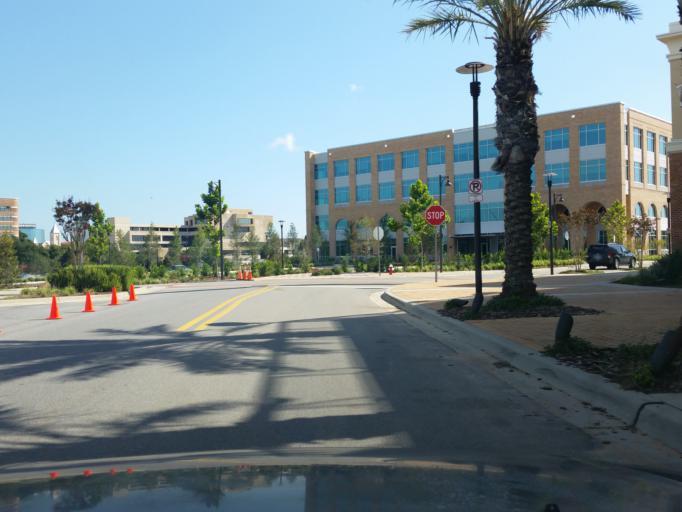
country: US
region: Florida
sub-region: Escambia County
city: Pensacola
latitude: 30.4049
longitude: -87.2190
